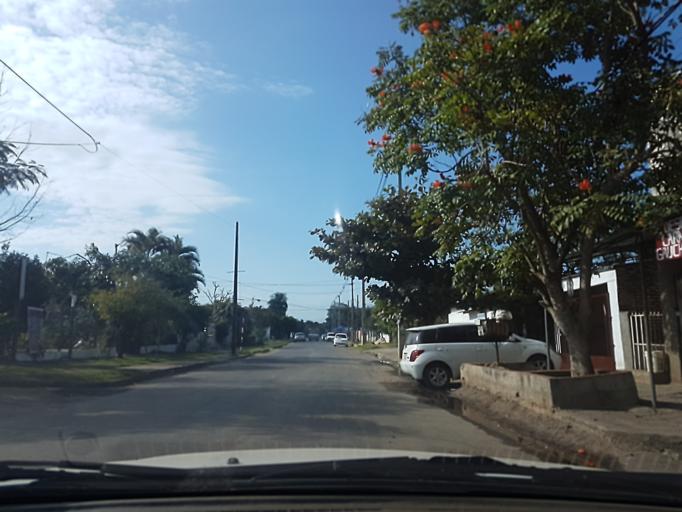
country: PY
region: Central
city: Colonia Mariano Roque Alonso
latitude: -25.2493
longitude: -57.5352
